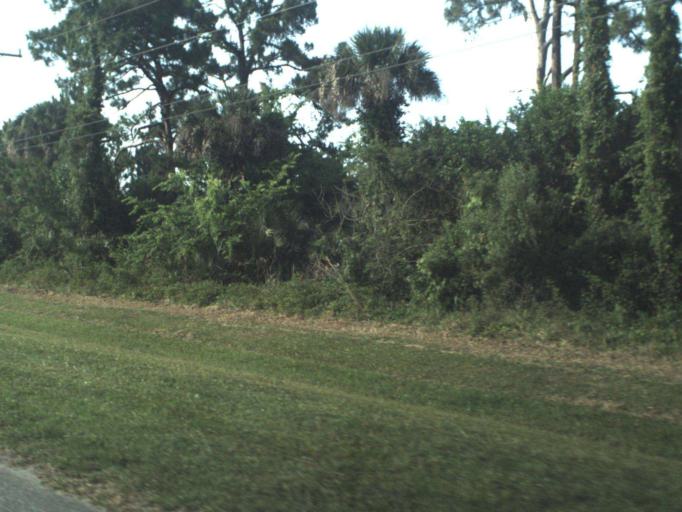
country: US
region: Florida
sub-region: Volusia County
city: Oak Hill
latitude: 28.9231
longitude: -80.8730
